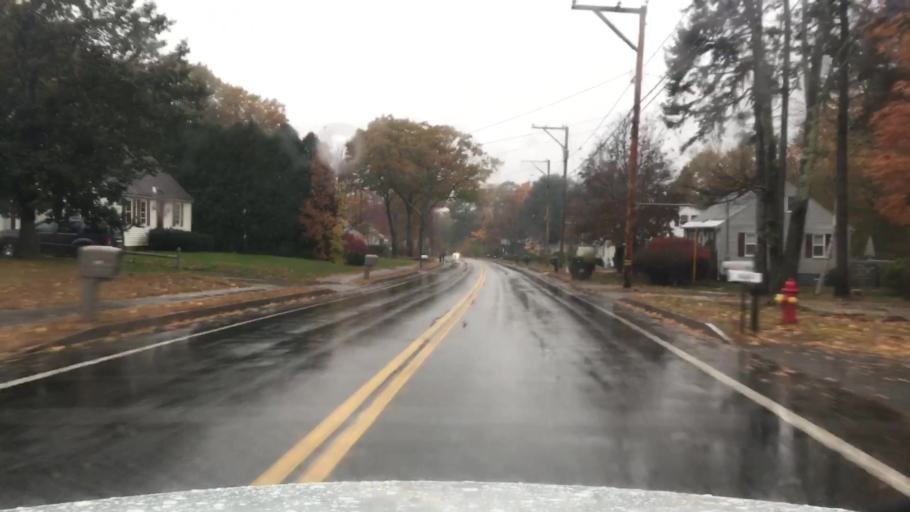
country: US
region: New Hampshire
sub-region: Strafford County
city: Rochester
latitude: 43.3233
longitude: -70.9504
